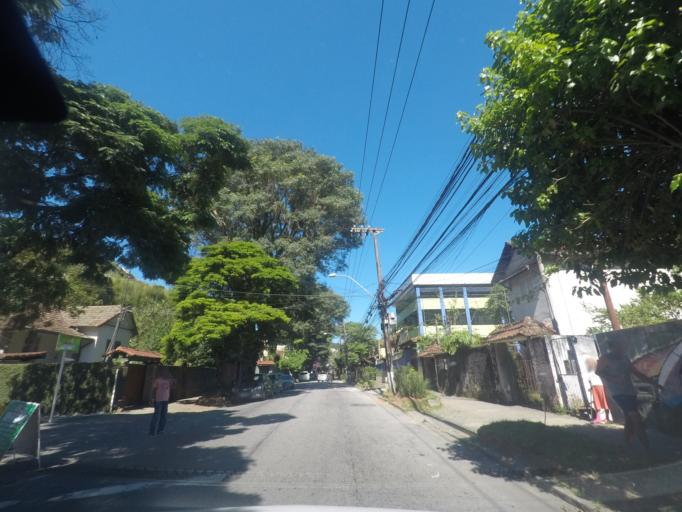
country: BR
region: Rio de Janeiro
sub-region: Petropolis
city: Petropolis
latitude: -22.5278
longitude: -43.1730
